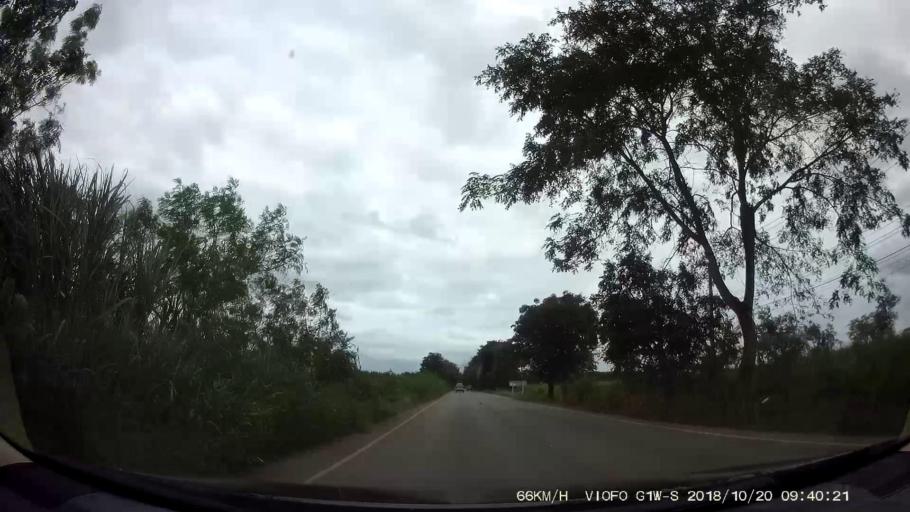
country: TH
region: Chaiyaphum
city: Kaset Sombun
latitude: 16.4421
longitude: 101.9619
